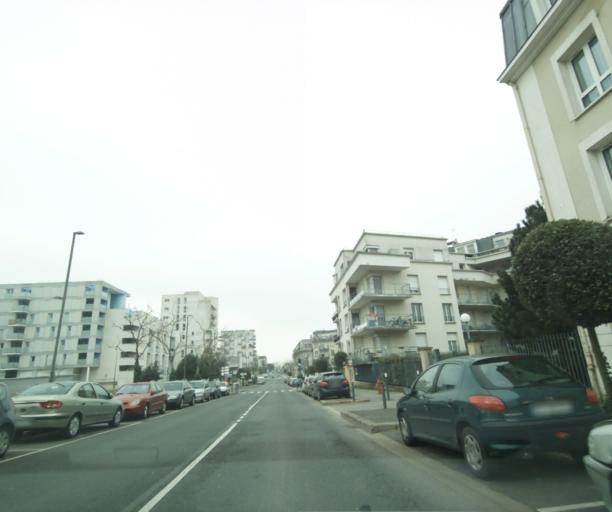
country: FR
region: Ile-de-France
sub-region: Departement du Val-d'Oise
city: Courdimanche
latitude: 49.0456
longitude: 2.0117
